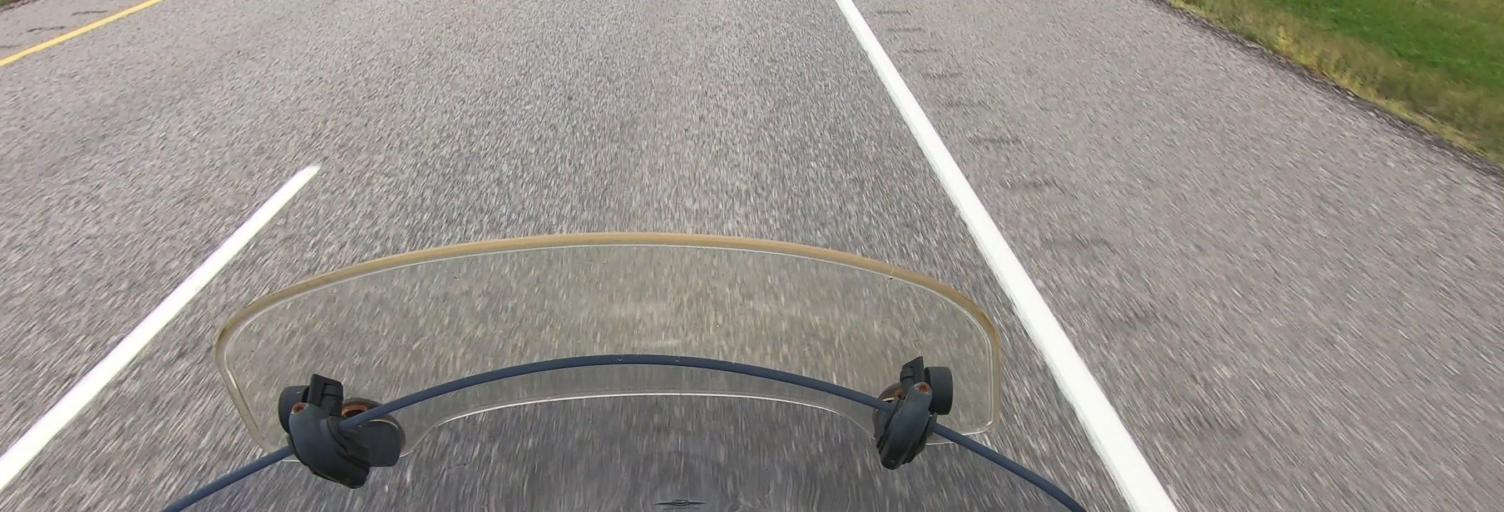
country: CA
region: Manitoba
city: Portage la Prairie
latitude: 49.9755
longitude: -98.6841
